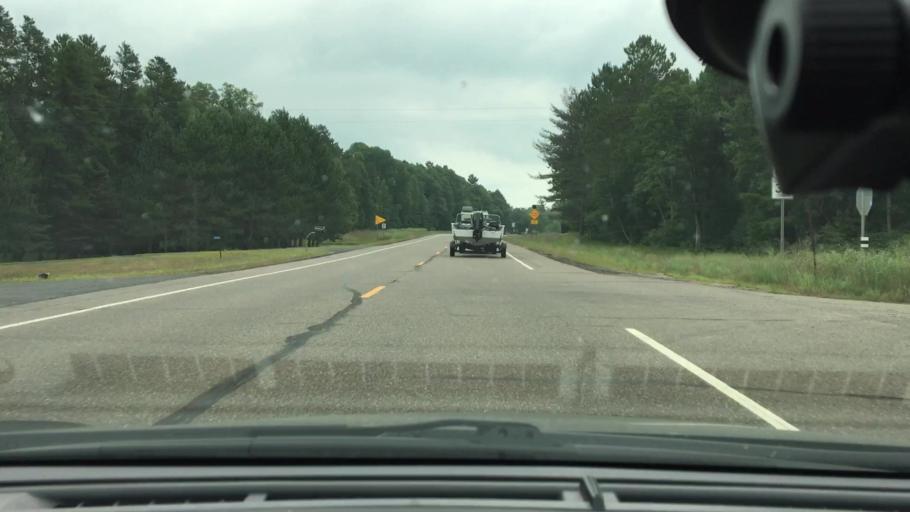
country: US
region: Minnesota
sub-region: Crow Wing County
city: Crosby
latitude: 46.5432
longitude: -93.9545
